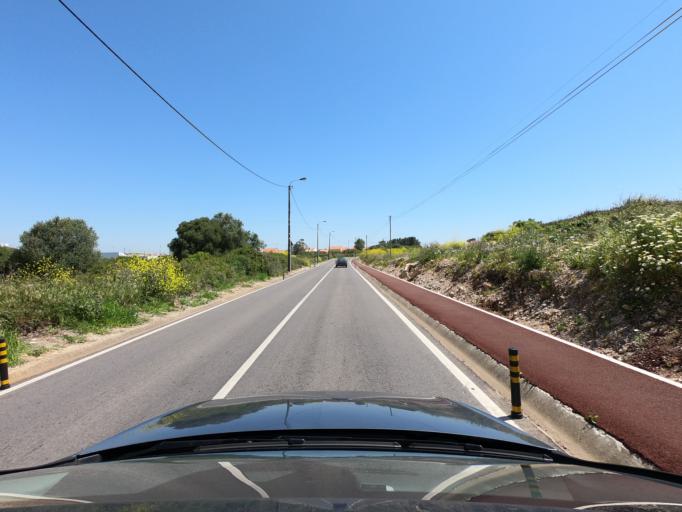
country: PT
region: Lisbon
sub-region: Cascais
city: Sao Domingos de Rana
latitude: 38.7329
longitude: -9.3478
